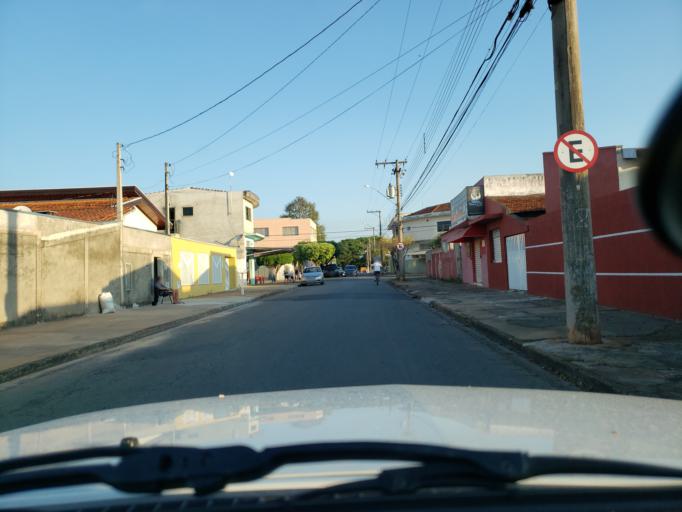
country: BR
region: Sao Paulo
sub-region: Moji-Guacu
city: Mogi-Gaucu
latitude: -22.3447
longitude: -46.9380
